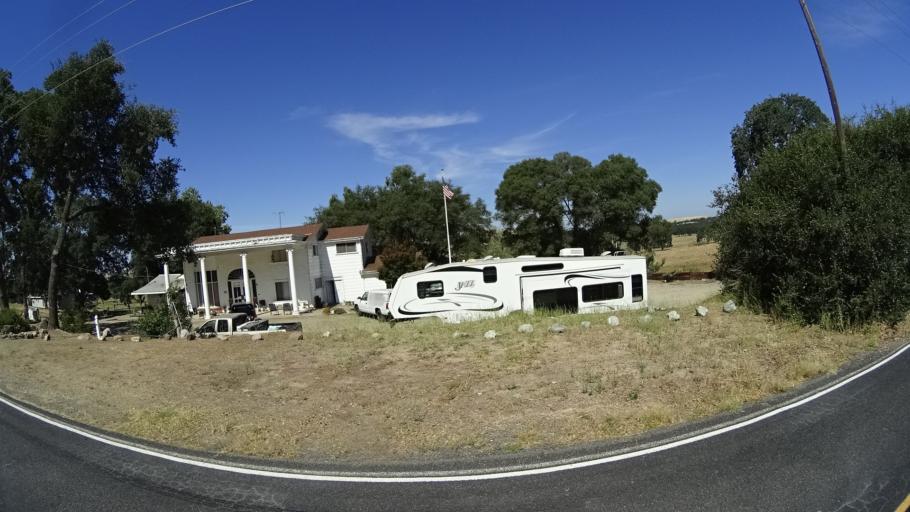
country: US
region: California
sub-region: Calaveras County
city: Rancho Calaveras
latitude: 38.1216
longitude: -120.9265
